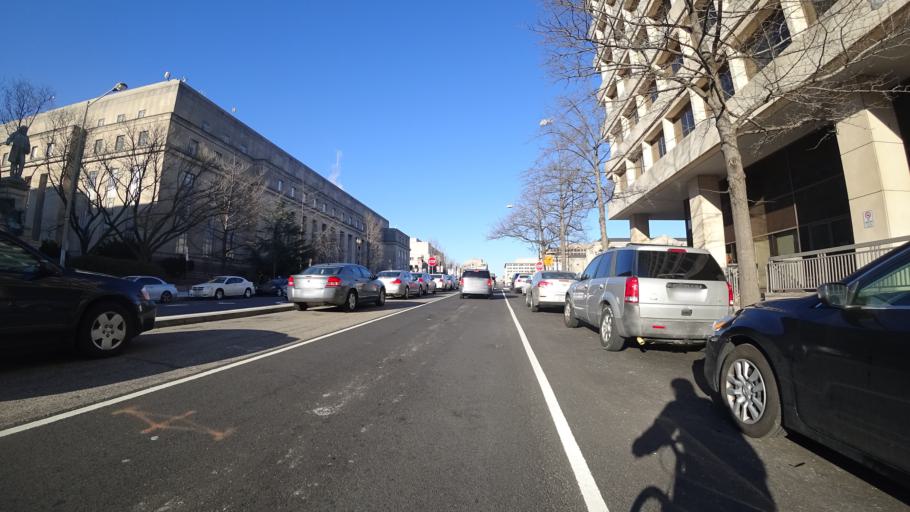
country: US
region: Washington, D.C.
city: Washington, D.C.
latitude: 38.8949
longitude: -77.0156
